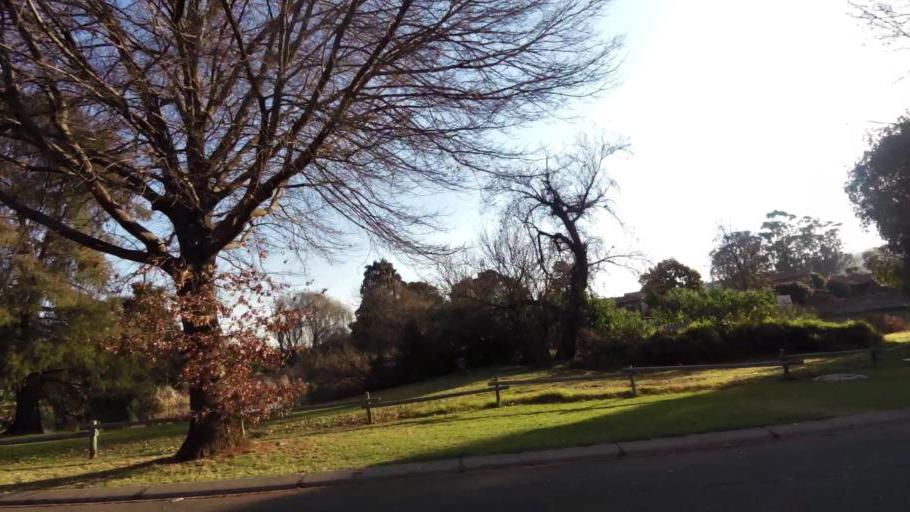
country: ZA
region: Gauteng
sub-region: City of Johannesburg Metropolitan Municipality
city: Johannesburg
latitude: -26.1598
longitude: 27.9804
